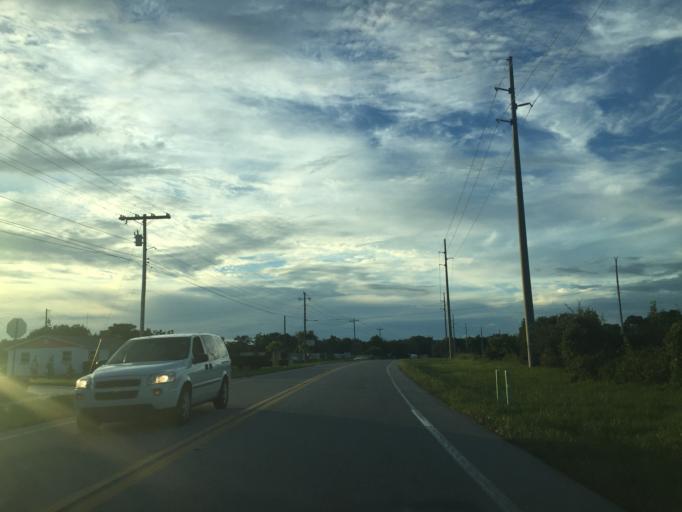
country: US
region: Florida
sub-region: Lake County
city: Tavares
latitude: 28.7785
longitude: -81.7455
